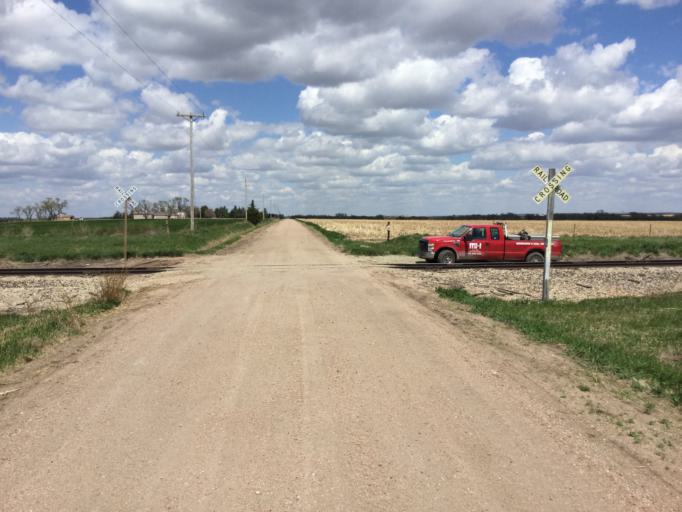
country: US
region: Kansas
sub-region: Phillips County
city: Phillipsburg
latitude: 39.7635
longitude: -99.0853
